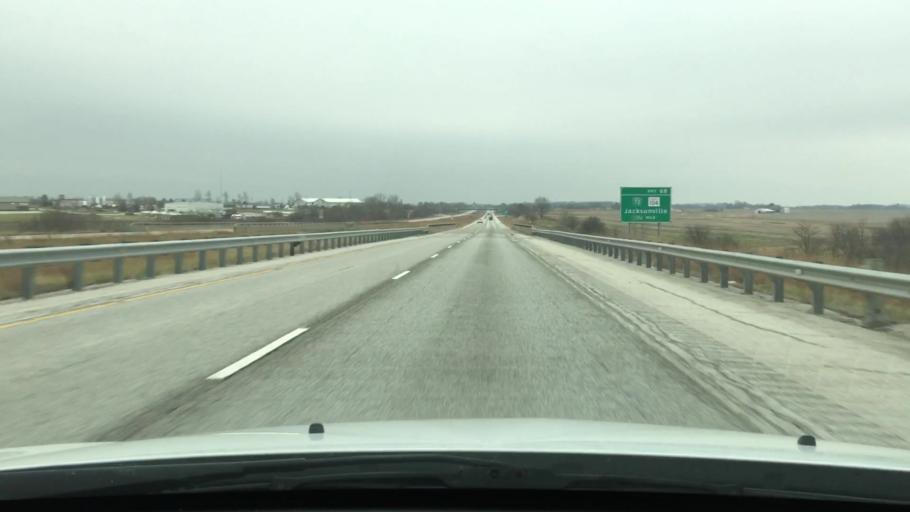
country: US
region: Illinois
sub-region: Morgan County
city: South Jacksonville
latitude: 39.7131
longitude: -90.1777
